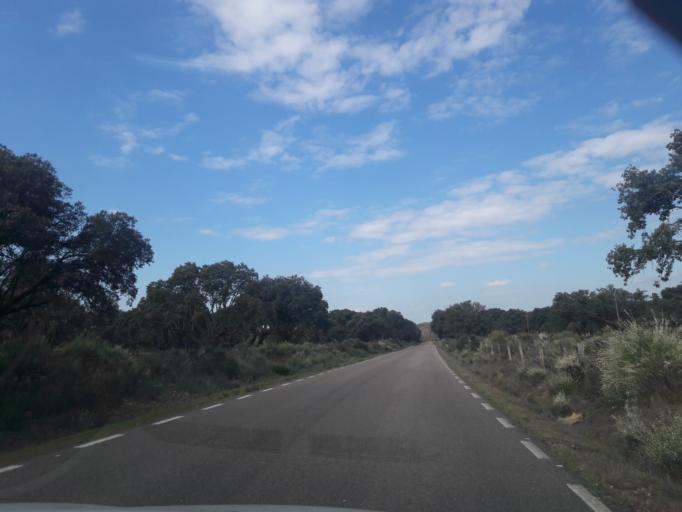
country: ES
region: Castille and Leon
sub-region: Provincia de Salamanca
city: Zamarra
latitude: 40.5608
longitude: -6.4655
